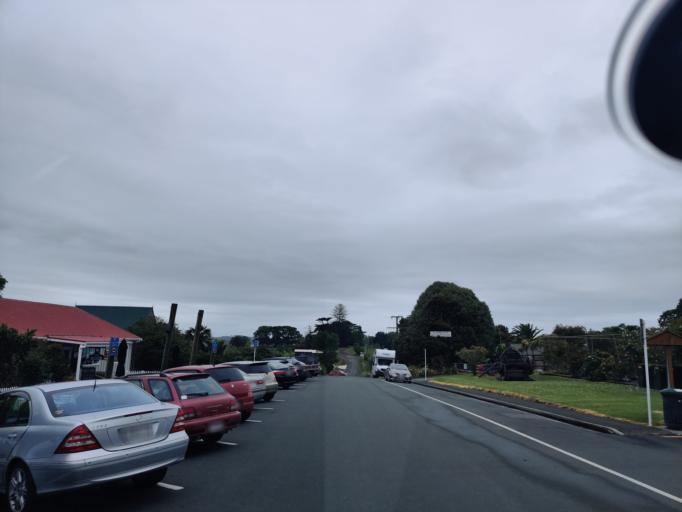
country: NZ
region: Northland
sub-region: Whangarei
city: Ruakaka
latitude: -36.1298
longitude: 174.1858
